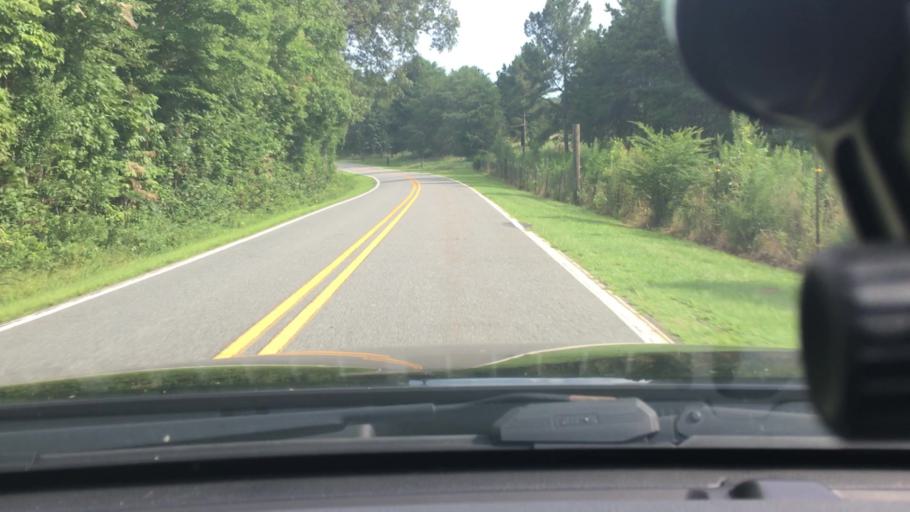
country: US
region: North Carolina
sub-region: Rutherford County
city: Rutherfordton
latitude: 35.4012
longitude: -81.9738
